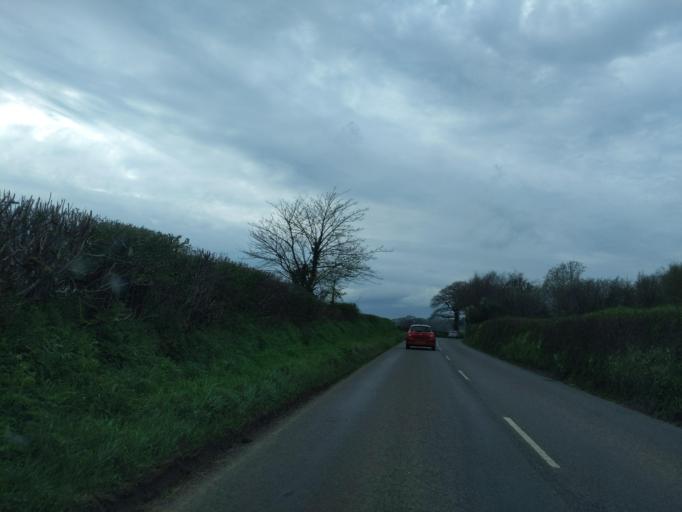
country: GB
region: England
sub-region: Devon
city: Winkleigh
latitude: 50.8506
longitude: -3.9301
